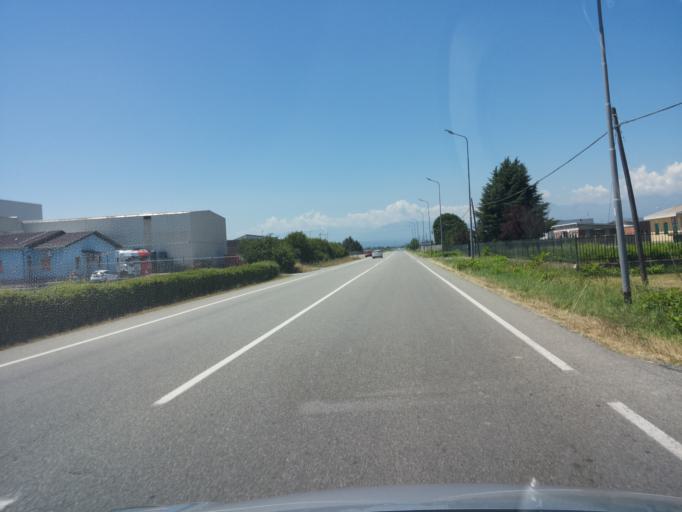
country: IT
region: Piedmont
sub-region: Provincia di Vercelli
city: Formigliana
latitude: 45.4311
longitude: 8.2821
